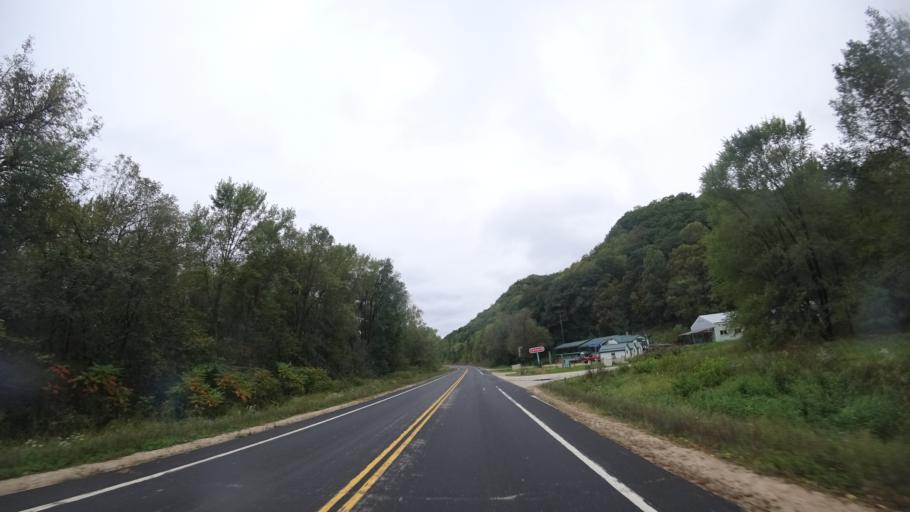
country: US
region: Wisconsin
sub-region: Grant County
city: Boscobel
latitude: 43.1766
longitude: -90.6881
